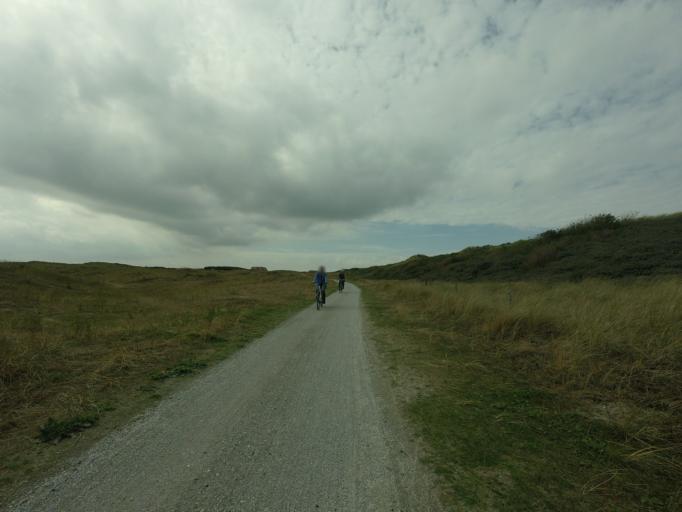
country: NL
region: Friesland
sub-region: Gemeente Ameland
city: Nes
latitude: 53.4614
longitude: 5.8149
